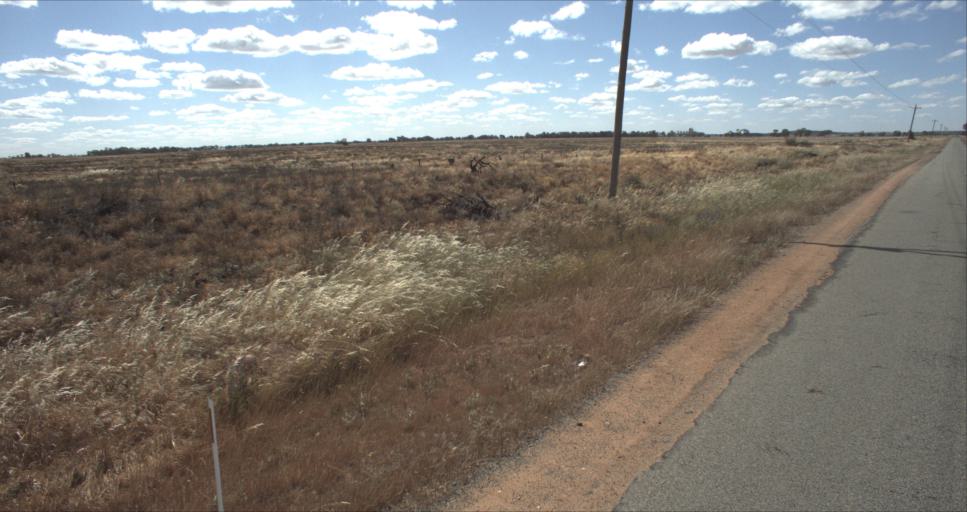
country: AU
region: New South Wales
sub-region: Leeton
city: Leeton
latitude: -34.4790
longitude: 146.2495
